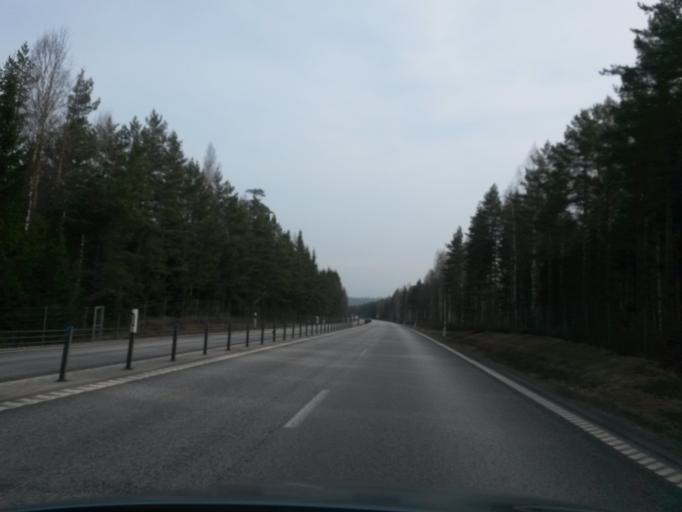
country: SE
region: Vaestra Goetaland
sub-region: Gullspangs Kommun
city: Anderstorp
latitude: 58.9211
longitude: 14.4029
